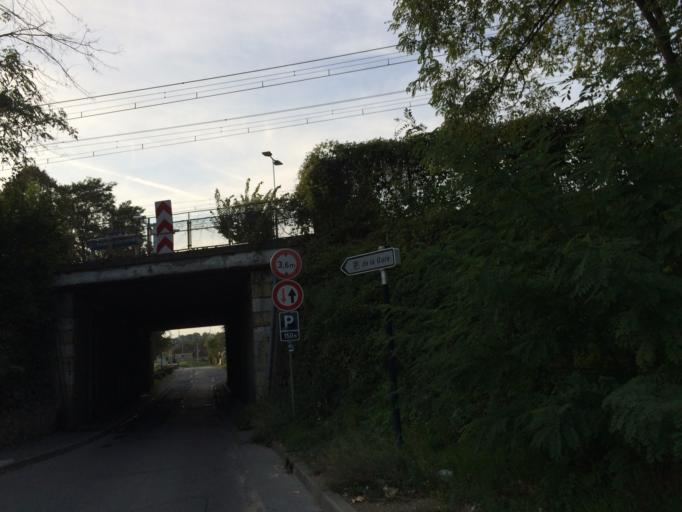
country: FR
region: Ile-de-France
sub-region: Departement de l'Essonne
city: Vigneux-sur-Seine
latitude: 48.7088
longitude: 2.4155
